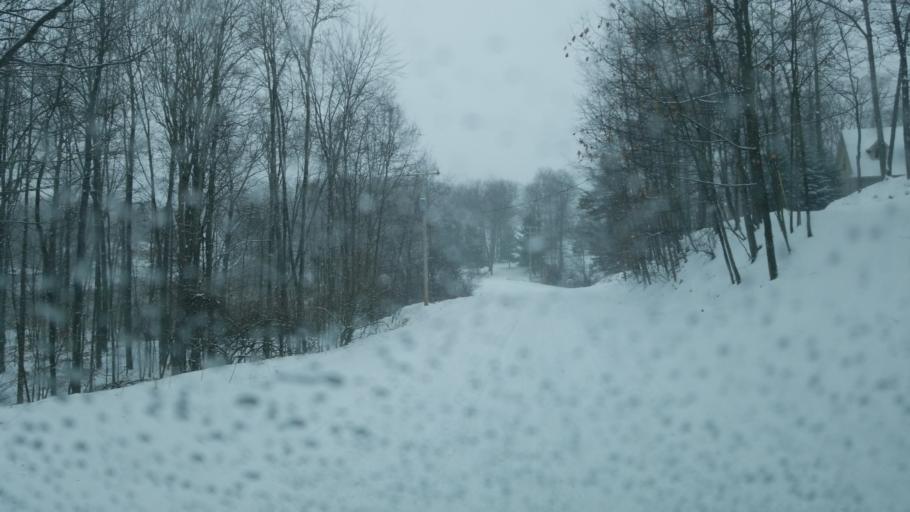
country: US
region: Michigan
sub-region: Mecosta County
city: Canadian Lakes
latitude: 43.6065
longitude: -85.3047
